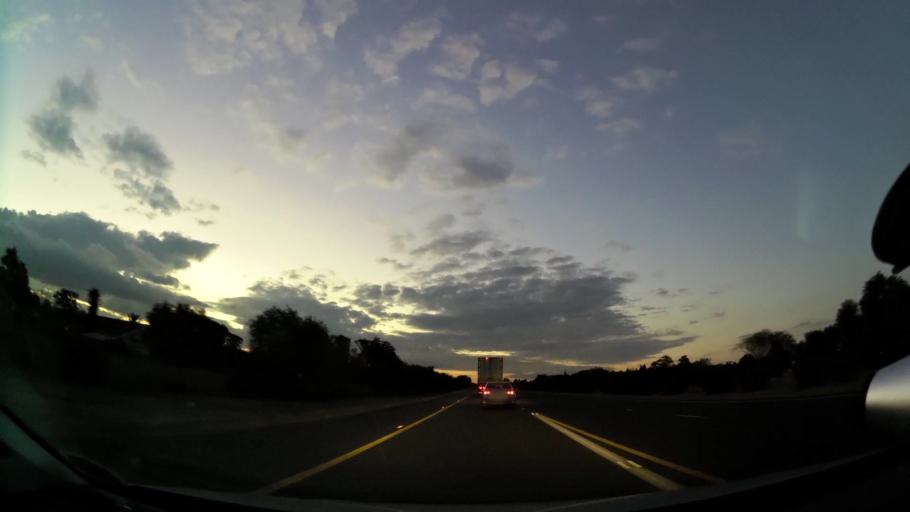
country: ZA
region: Orange Free State
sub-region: Mangaung Metropolitan Municipality
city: Bloemfontein
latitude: -29.1616
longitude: 26.1791
